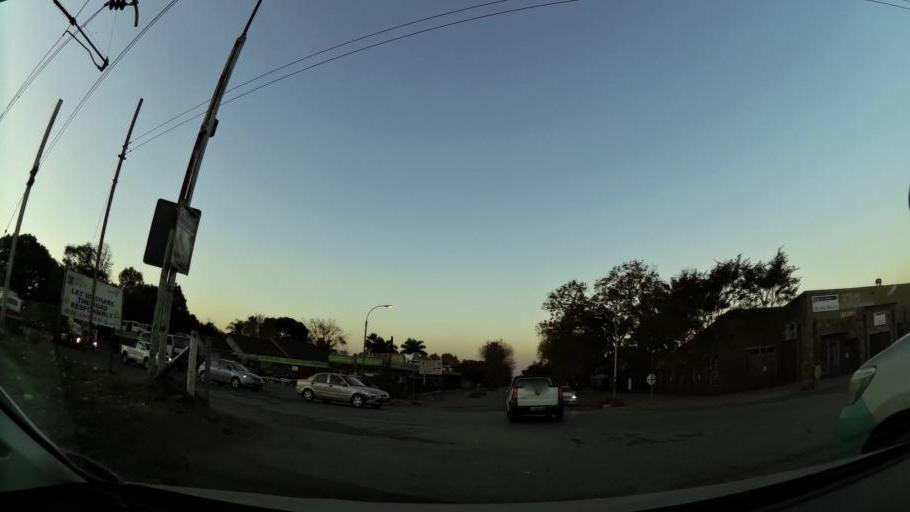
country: ZA
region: North-West
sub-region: Bojanala Platinum District Municipality
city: Rustenburg
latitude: -25.6633
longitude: 27.2499
